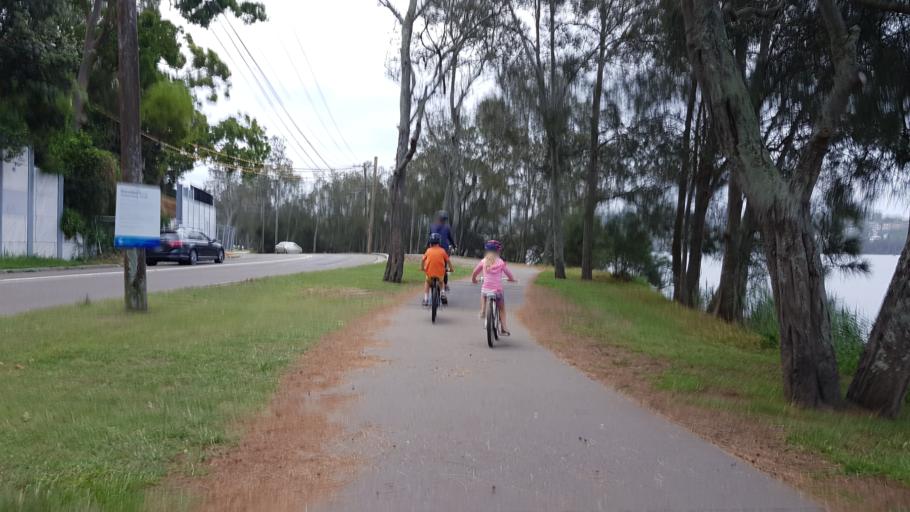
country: AU
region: New South Wales
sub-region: Warringah
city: Narrabeen
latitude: -33.7207
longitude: 151.2916
